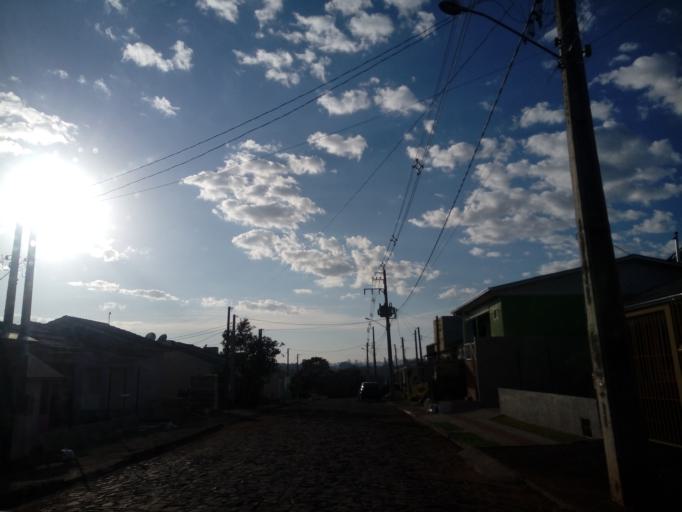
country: BR
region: Santa Catarina
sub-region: Chapeco
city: Chapeco
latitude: -27.1093
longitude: -52.6686
